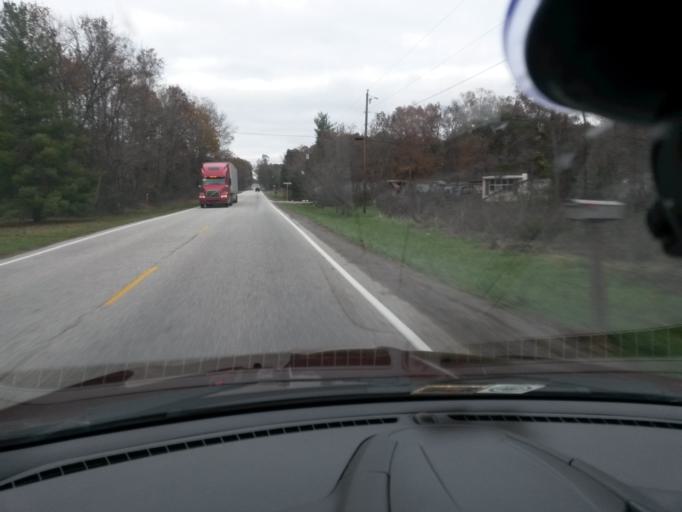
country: US
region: Virginia
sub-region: Rockbridge County
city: Glasgow
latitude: 37.6539
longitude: -79.4255
